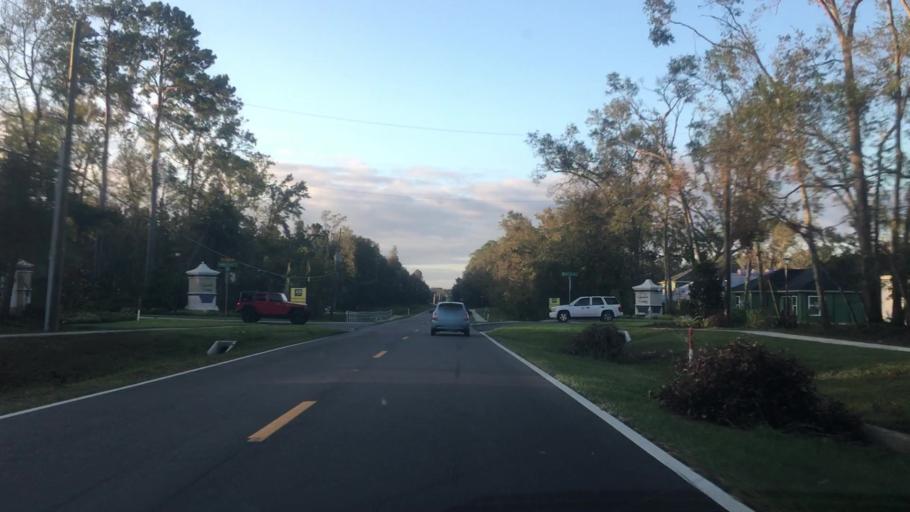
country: US
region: Florida
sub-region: Duval County
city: Jacksonville
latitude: 30.4678
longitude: -81.5794
